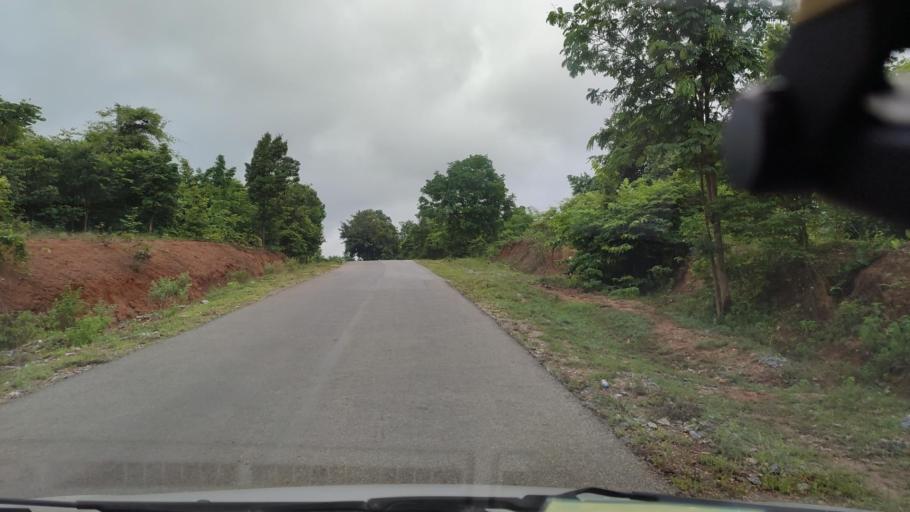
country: MM
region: Mandalay
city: Nay Pyi Taw
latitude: 19.9832
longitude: 95.9766
